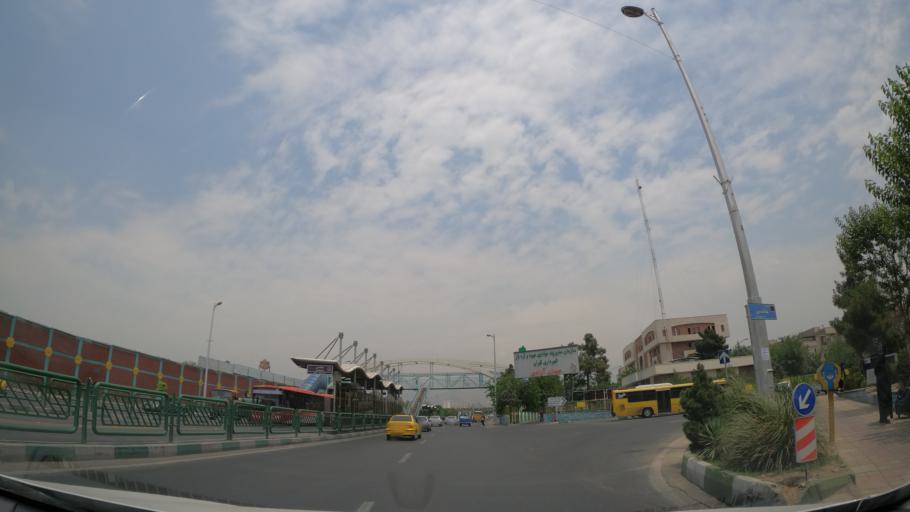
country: IR
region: Tehran
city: Tehran
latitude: 35.6884
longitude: 51.3408
